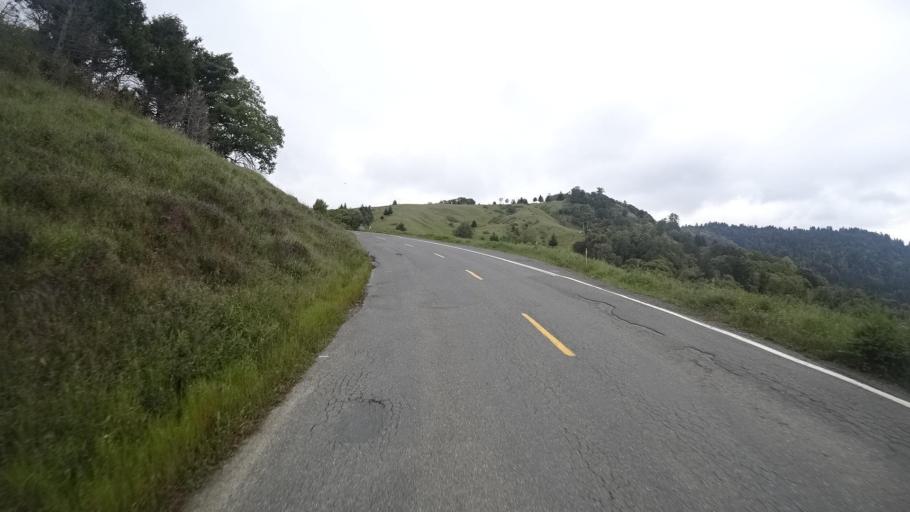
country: US
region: California
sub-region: Humboldt County
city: Redway
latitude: 40.1139
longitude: -123.7588
